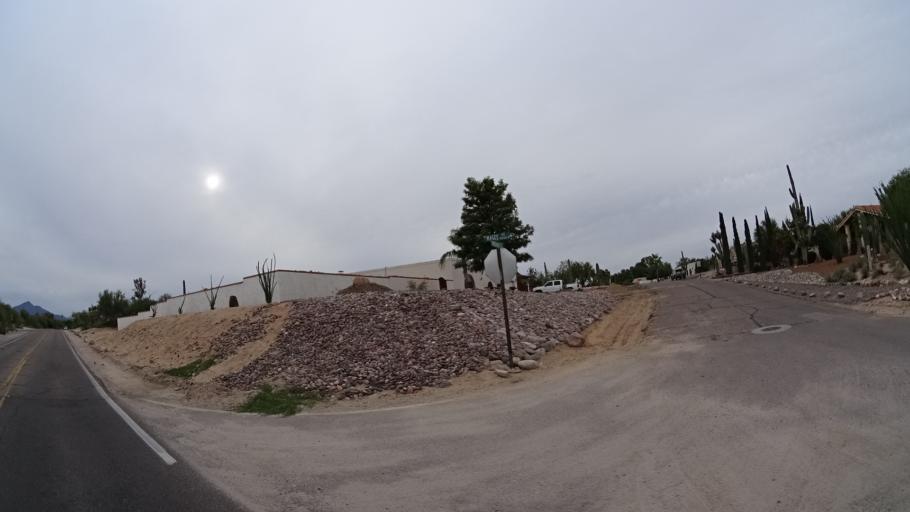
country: US
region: Arizona
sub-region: Pima County
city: Casas Adobes
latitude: 32.3535
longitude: -111.0340
